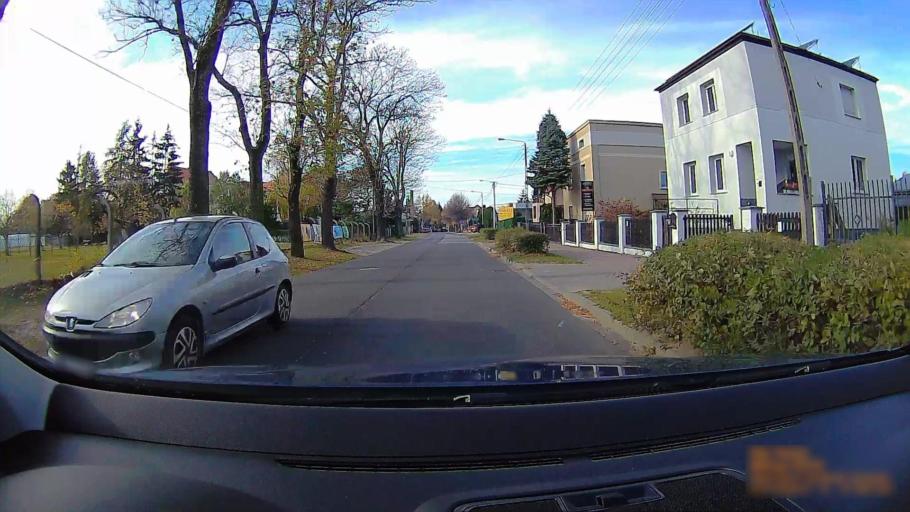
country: PL
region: Greater Poland Voivodeship
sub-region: Powiat ostrzeszowski
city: Ostrzeszow
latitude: 51.4322
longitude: 17.9337
